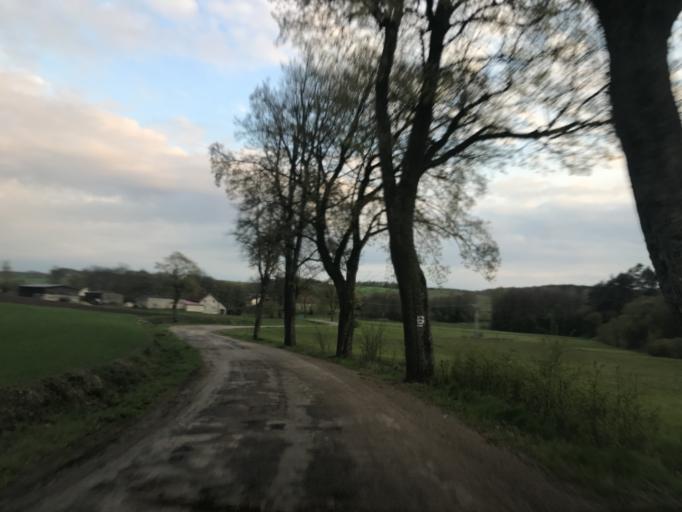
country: PL
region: Warmian-Masurian Voivodeship
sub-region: Powiat ilawski
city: Lubawa
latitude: 53.5386
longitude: 19.8967
